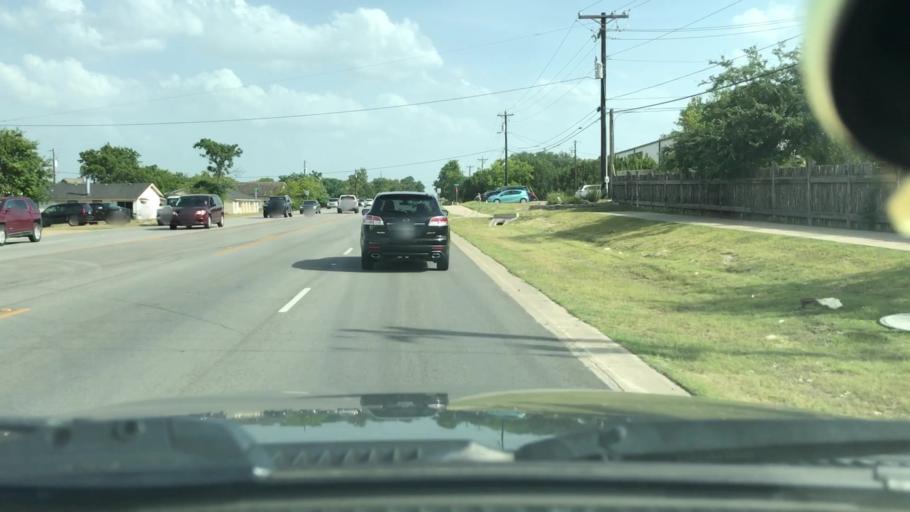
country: US
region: Texas
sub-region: Williamson County
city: Leander
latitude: 30.5476
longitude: -97.8525
